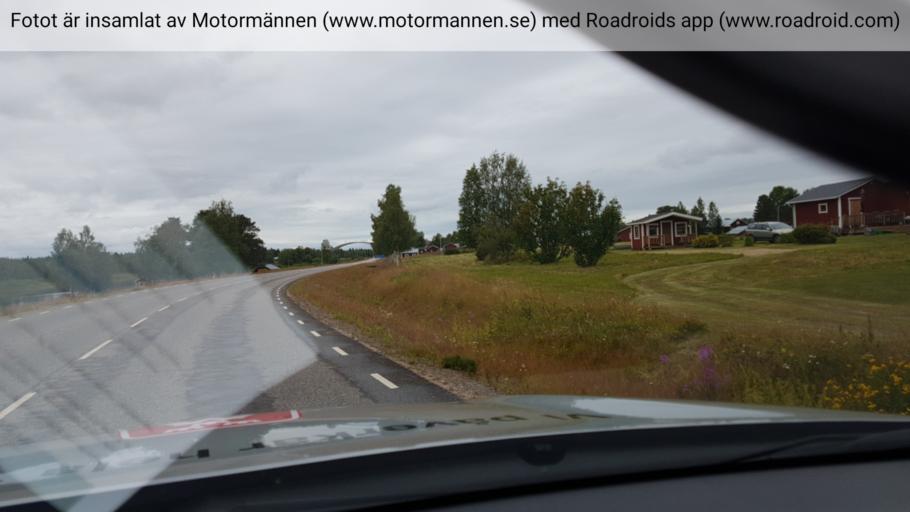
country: SE
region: Norrbotten
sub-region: Pajala Kommun
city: Pajala
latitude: 67.1623
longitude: 22.6261
